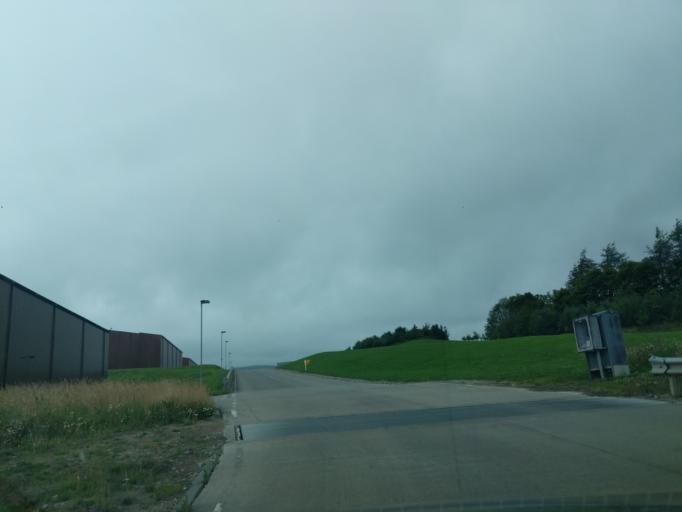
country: GB
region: Scotland
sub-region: Moray
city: Rothes
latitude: 57.4893
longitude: -3.2062
